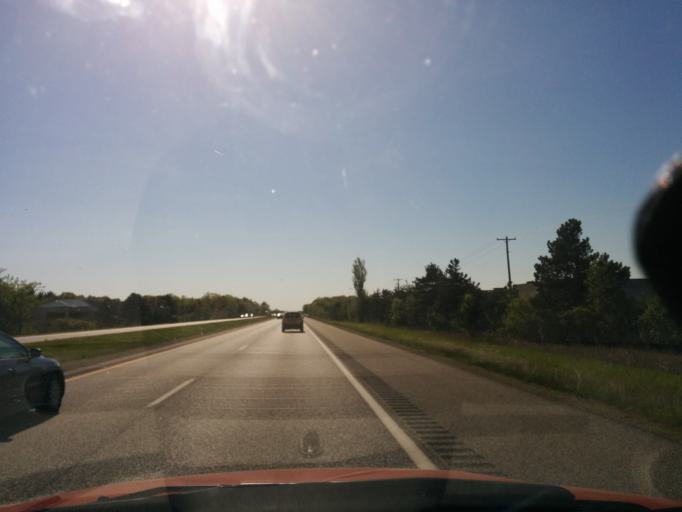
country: US
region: Michigan
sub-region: Midland County
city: Midland
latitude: 43.6559
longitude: -84.2304
